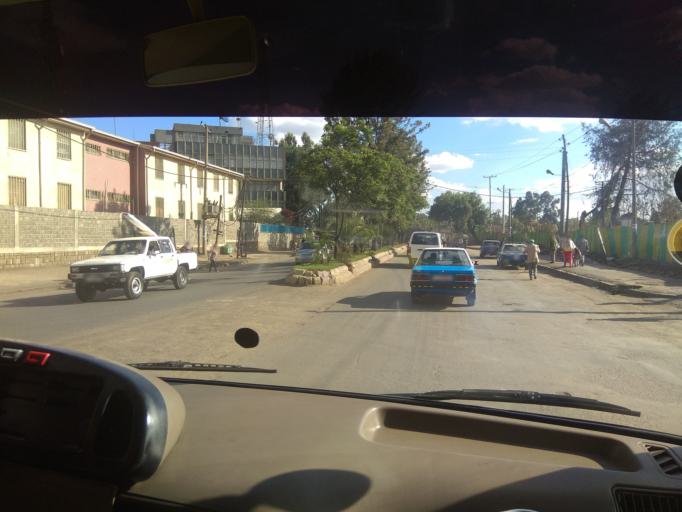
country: ET
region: Adis Abeba
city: Addis Ababa
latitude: 9.0200
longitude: 38.7470
